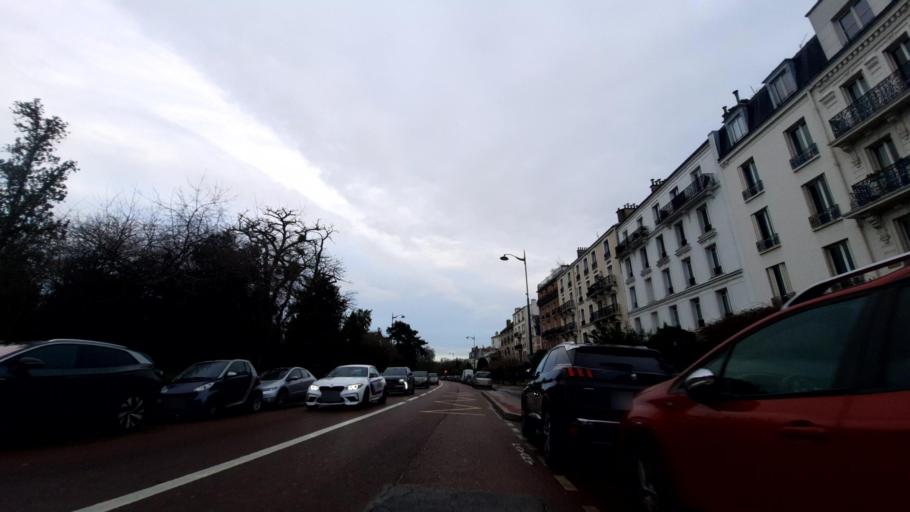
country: FR
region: Ile-de-France
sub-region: Departement du Val-de-Marne
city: Charenton-le-Pont
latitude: 48.8247
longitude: 2.4127
